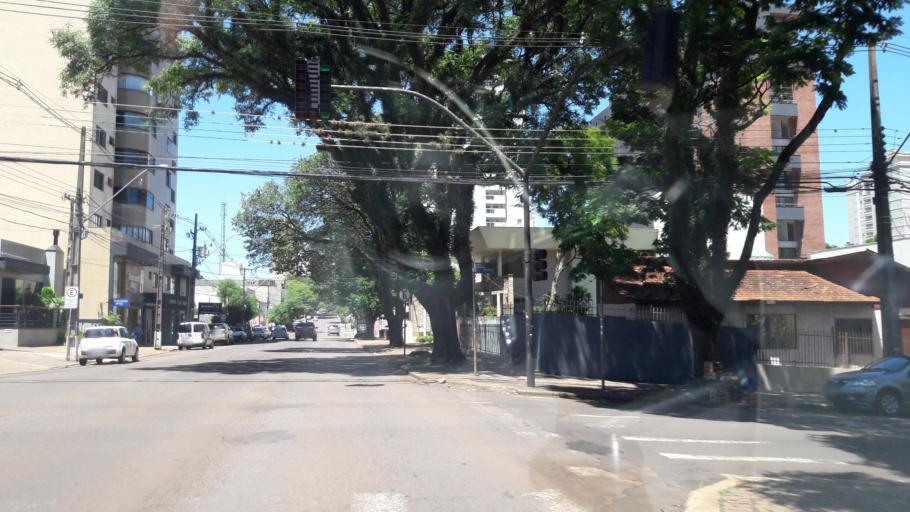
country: BR
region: Parana
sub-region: Cascavel
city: Cascavel
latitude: -24.9493
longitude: -53.4465
